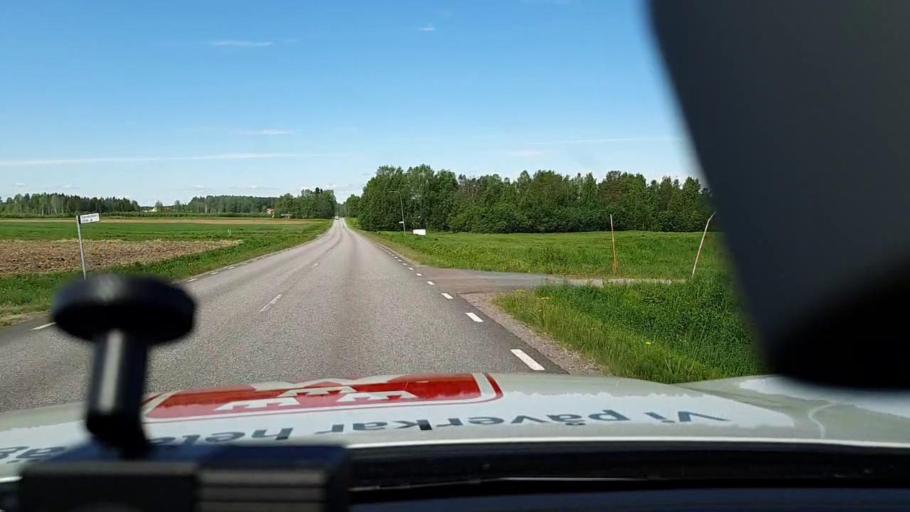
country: SE
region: Norrbotten
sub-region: Lulea Kommun
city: Sodra Sunderbyn
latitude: 65.6524
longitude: 21.8634
